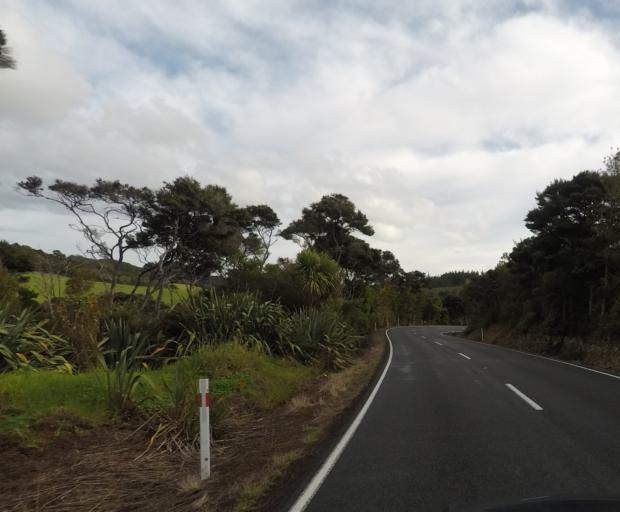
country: NZ
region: Northland
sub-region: Whangarei
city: Ruakaka
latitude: -36.0549
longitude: 174.5510
